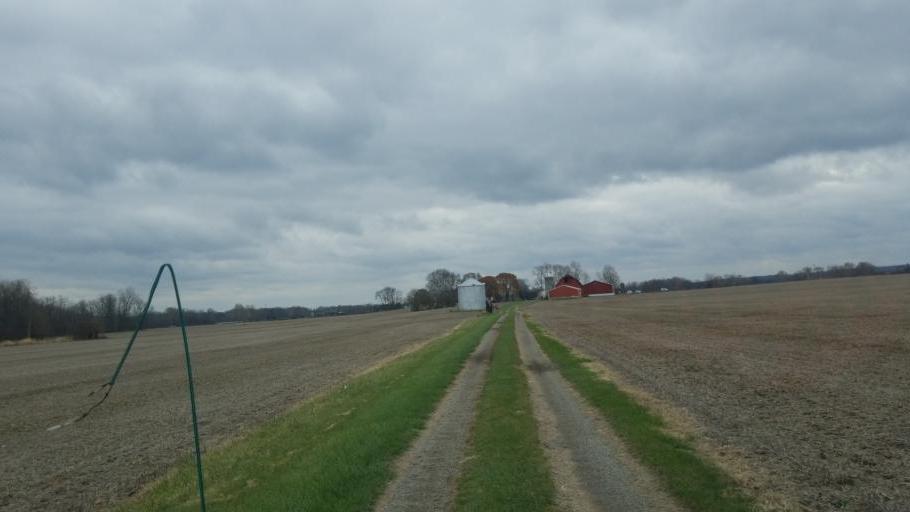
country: US
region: Ohio
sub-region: Knox County
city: Fredericktown
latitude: 40.4385
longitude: -82.5139
